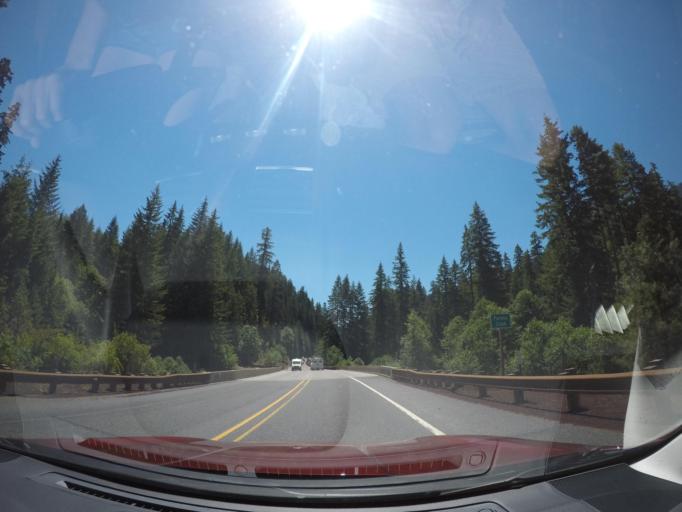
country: US
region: Oregon
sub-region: Linn County
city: Mill City
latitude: 44.6634
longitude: -121.9568
